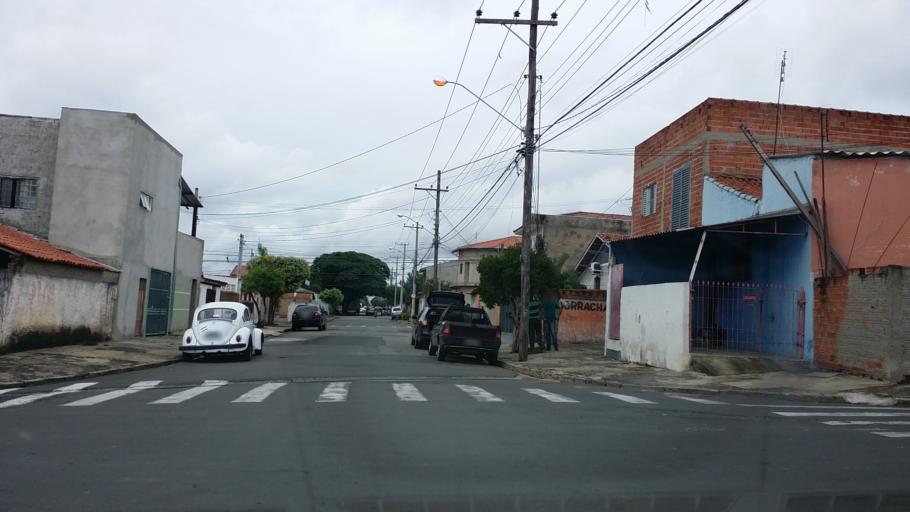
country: BR
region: Sao Paulo
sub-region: Indaiatuba
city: Indaiatuba
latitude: -23.1206
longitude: -47.2294
